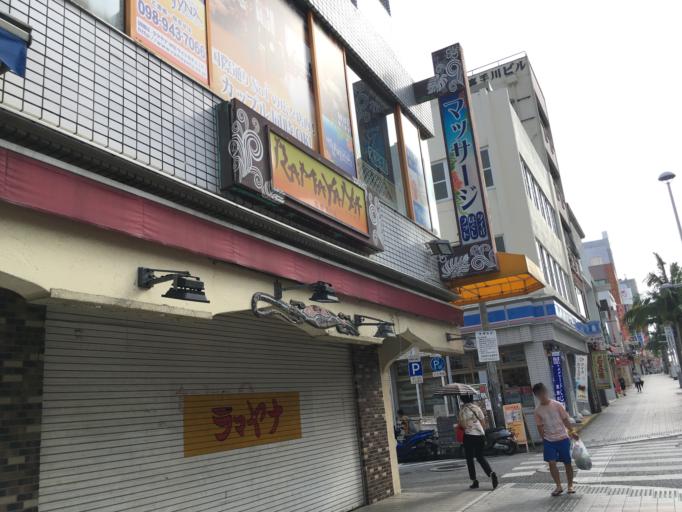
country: JP
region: Okinawa
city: Naha-shi
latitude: 26.2144
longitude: 127.6831
